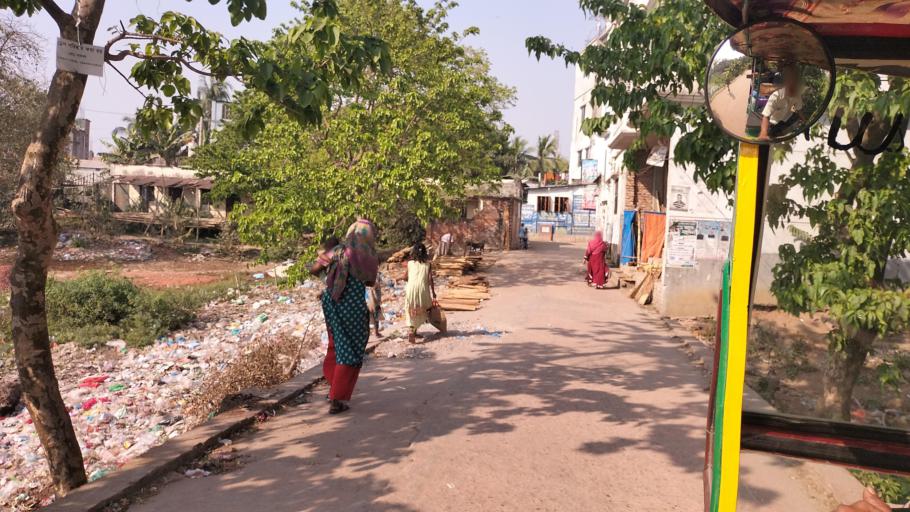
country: BD
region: Dhaka
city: Azimpur
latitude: 23.7960
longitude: 90.3374
